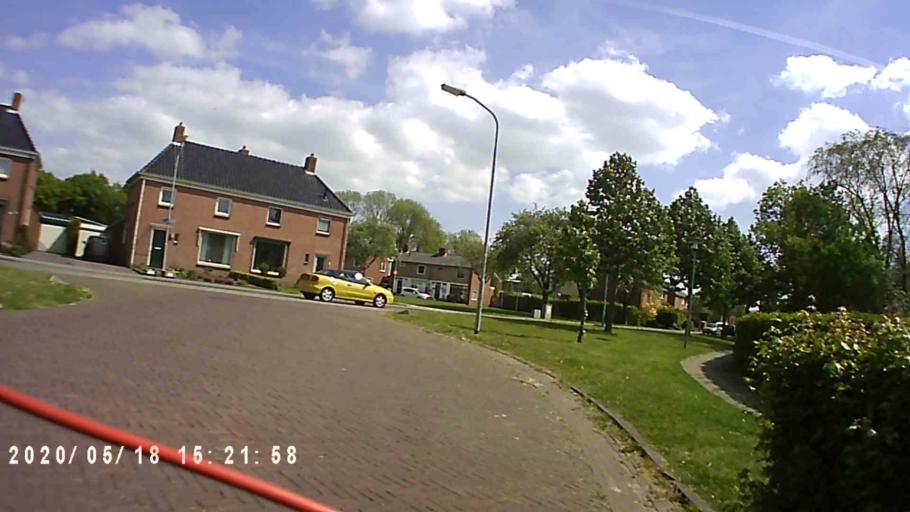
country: NL
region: Groningen
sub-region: Gemeente Winsum
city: Winsum
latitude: 53.3284
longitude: 6.5191
